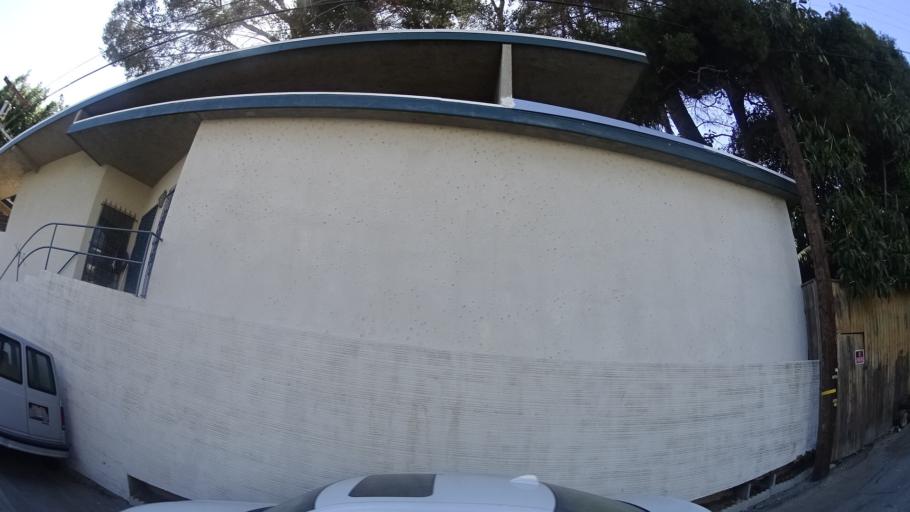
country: US
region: California
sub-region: Los Angeles County
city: West Hollywood
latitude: 34.1013
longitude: -118.3814
